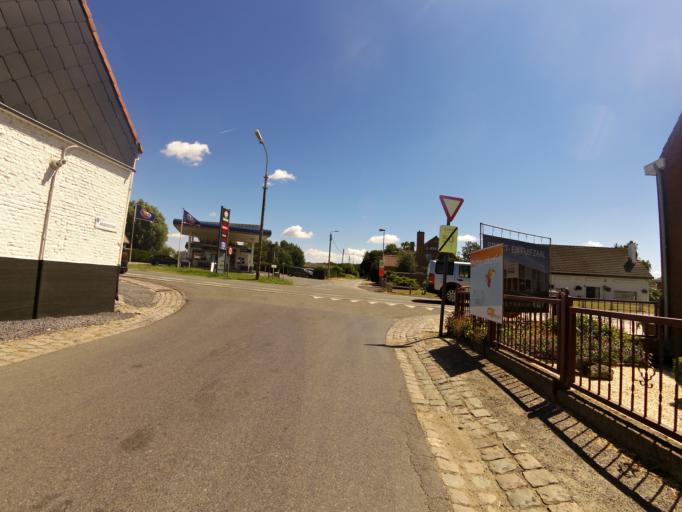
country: BE
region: Flanders
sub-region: Provincie West-Vlaanderen
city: Ichtegem
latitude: 51.0814
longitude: 3.0306
